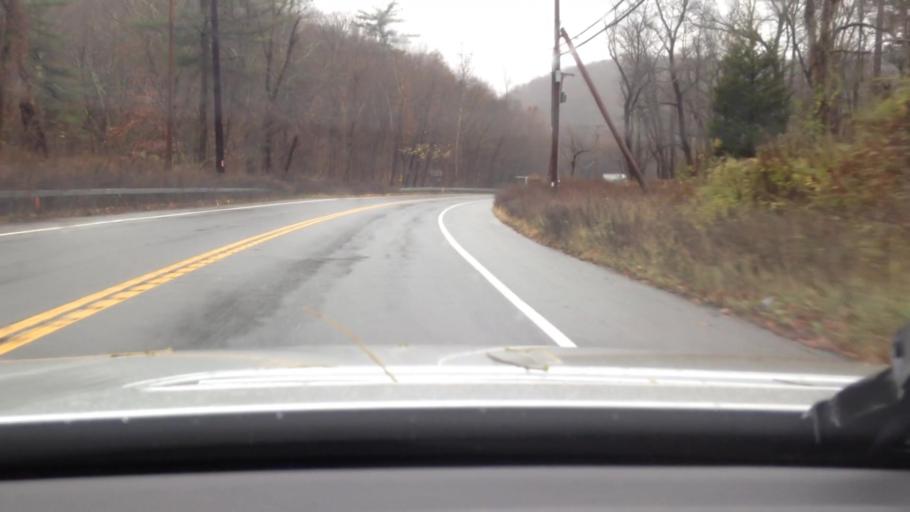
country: US
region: New York
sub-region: Westchester County
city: Peekskill
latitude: 41.3294
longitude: -73.9259
